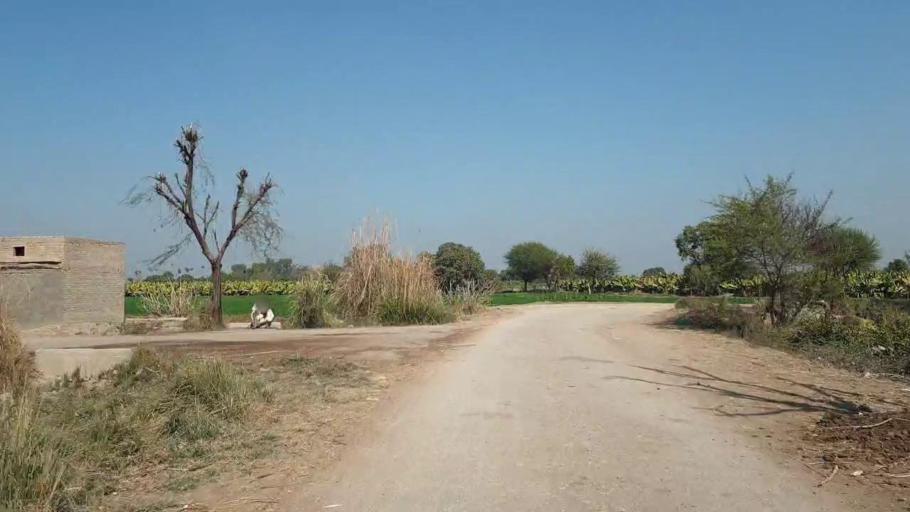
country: PK
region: Sindh
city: Shahdadpur
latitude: 25.9274
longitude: 68.5115
